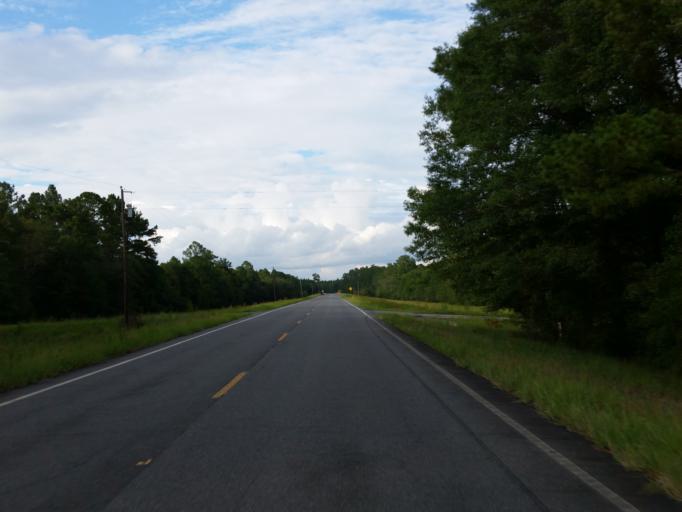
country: US
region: Florida
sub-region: Hamilton County
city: Jasper
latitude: 30.6527
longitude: -82.5666
